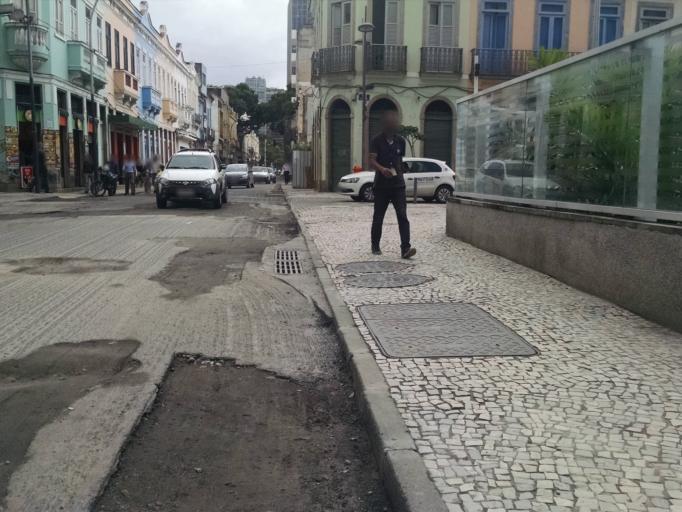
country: BR
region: Rio de Janeiro
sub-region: Rio De Janeiro
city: Rio de Janeiro
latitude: -22.9100
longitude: -43.1858
